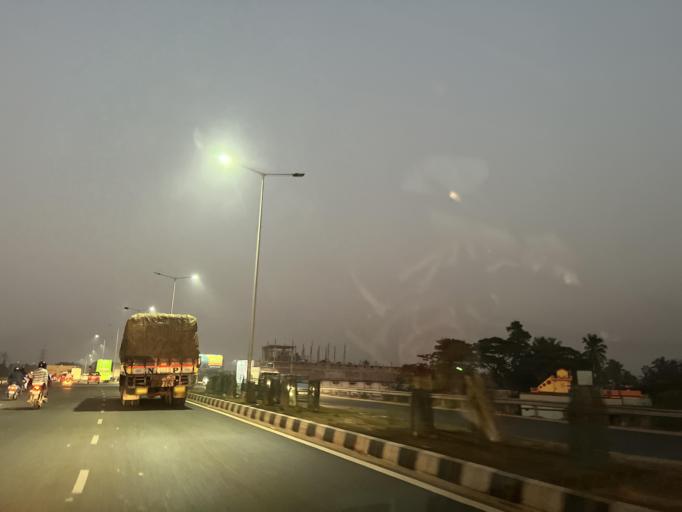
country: IN
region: Odisha
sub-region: Cuttack
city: Cuttack
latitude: 20.4322
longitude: 85.8798
